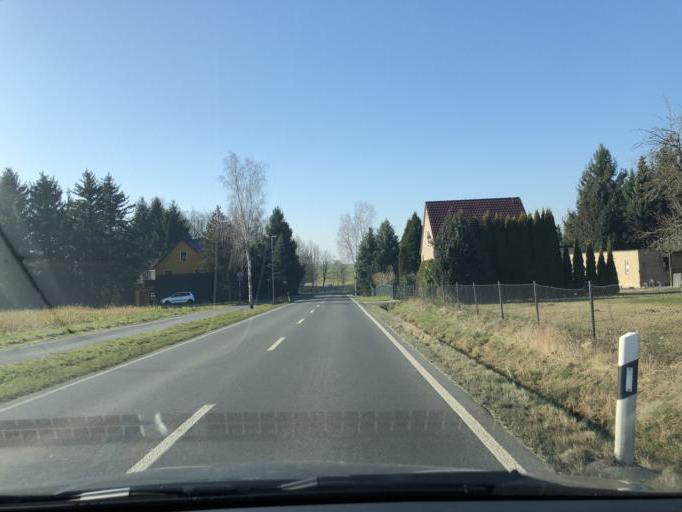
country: DE
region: Saxony
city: Ohorn
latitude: 51.1577
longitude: 14.0533
